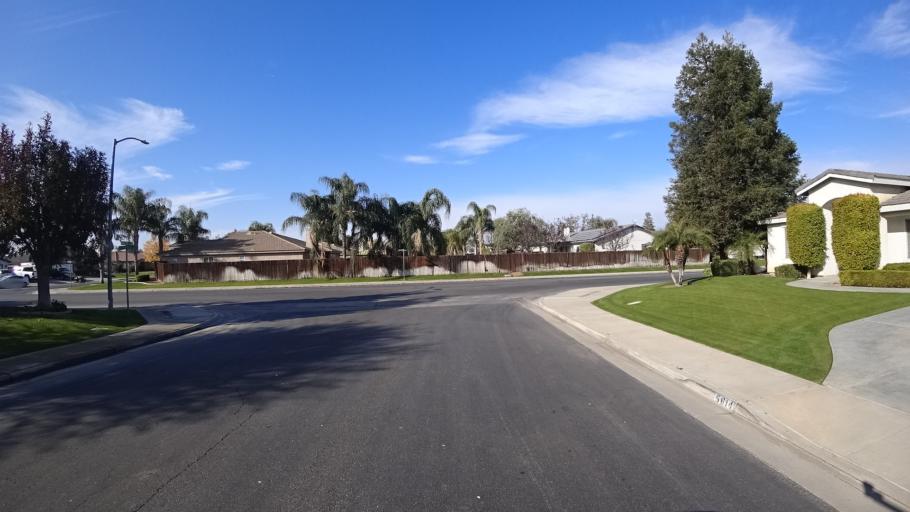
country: US
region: California
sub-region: Kern County
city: Oildale
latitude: 35.4043
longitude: -119.0652
